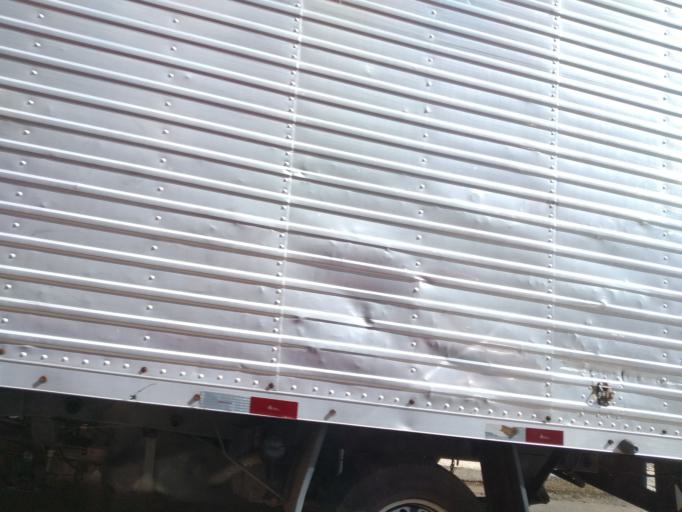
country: BR
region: Parana
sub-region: Pato Branco
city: Pato Branco
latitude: -26.2275
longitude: -52.6733
